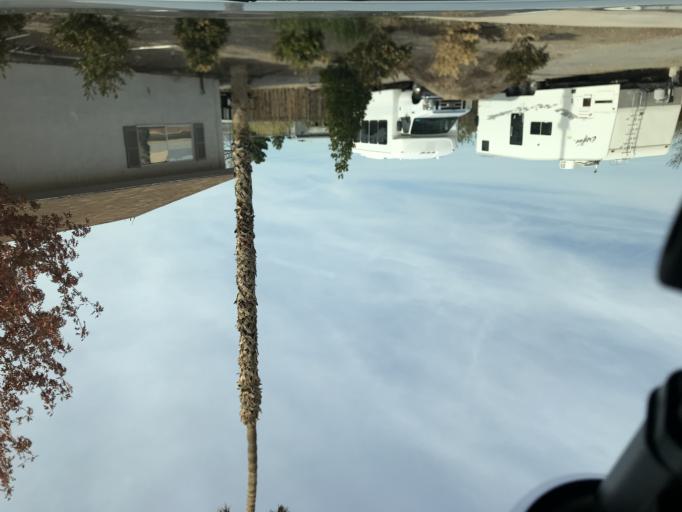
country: US
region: Nevada
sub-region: Clark County
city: Las Vegas
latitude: 36.1800
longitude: -115.1689
